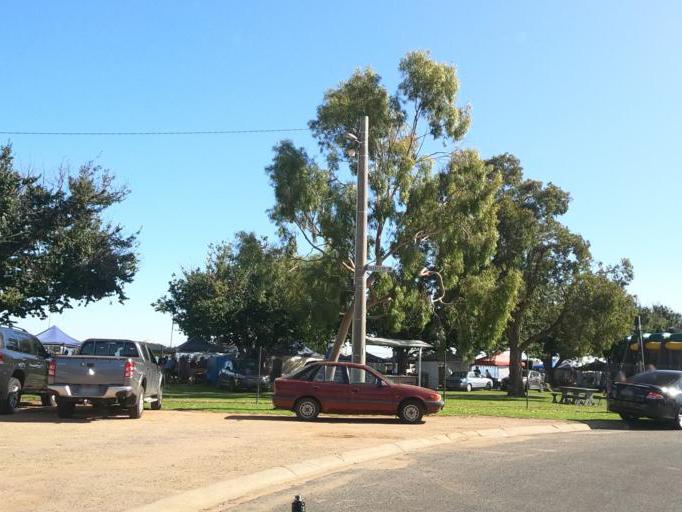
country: AU
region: Victoria
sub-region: Moira
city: Yarrawonga
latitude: -36.0080
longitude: 146.0077
